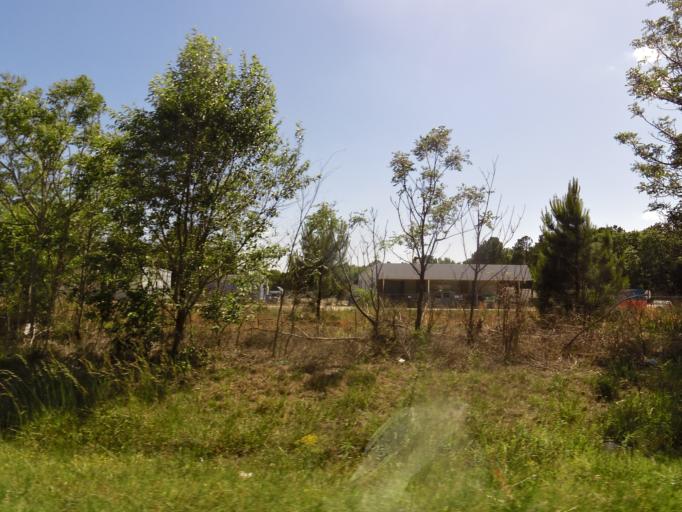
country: US
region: South Carolina
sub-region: Aiken County
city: Aiken
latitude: 33.5362
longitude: -81.6500
